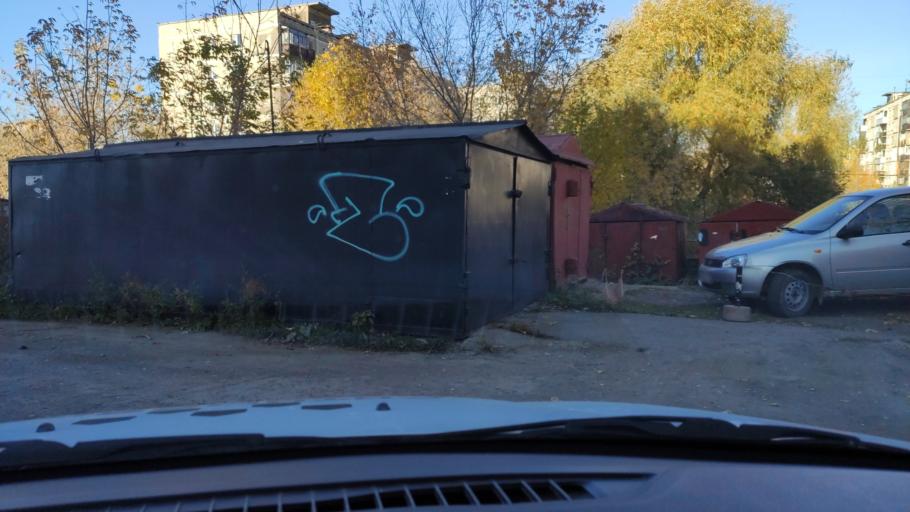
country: RU
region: Perm
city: Perm
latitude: 57.9672
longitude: 56.2131
